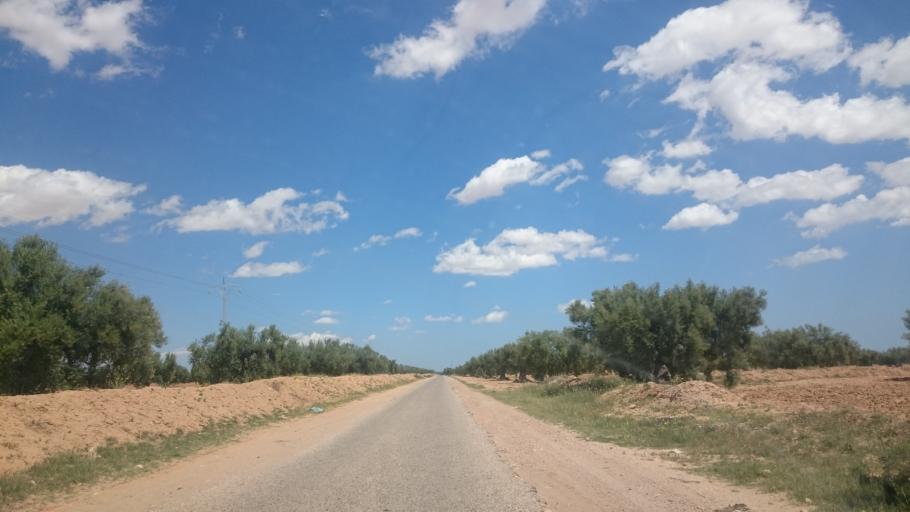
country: TN
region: Safaqis
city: Sfax
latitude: 34.6923
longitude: 10.5709
